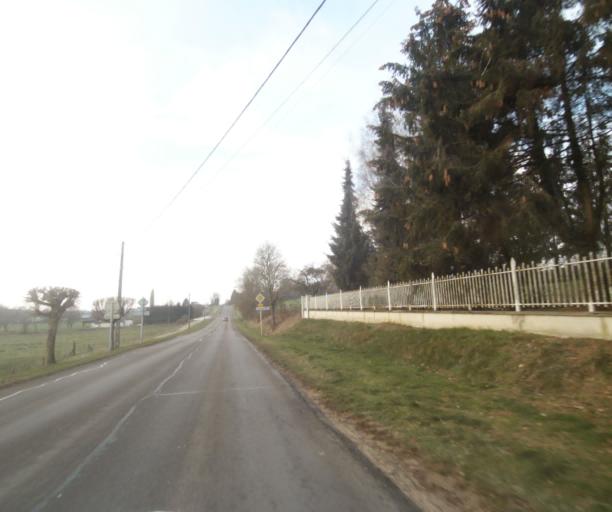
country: FR
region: Champagne-Ardenne
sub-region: Departement de la Haute-Marne
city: Chancenay
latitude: 48.6658
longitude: 4.9808
